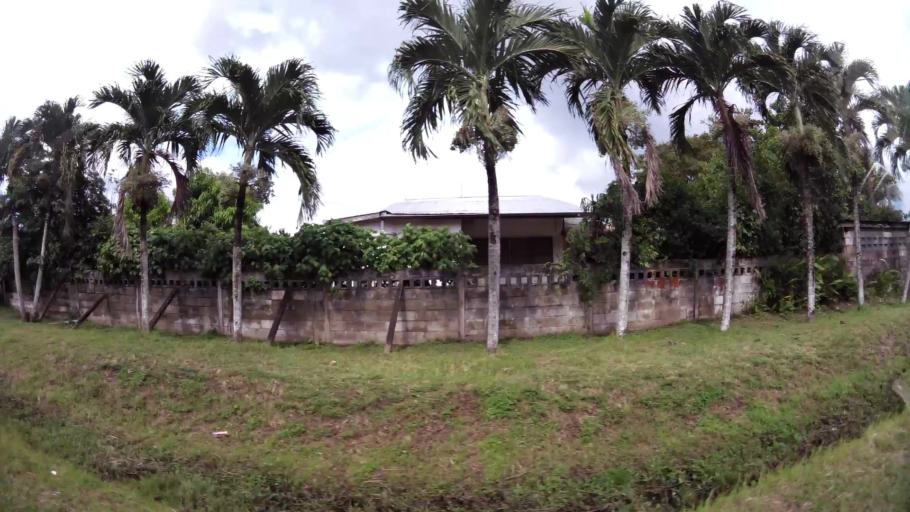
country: SR
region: Paramaribo
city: Paramaribo
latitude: 5.8432
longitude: -55.1929
